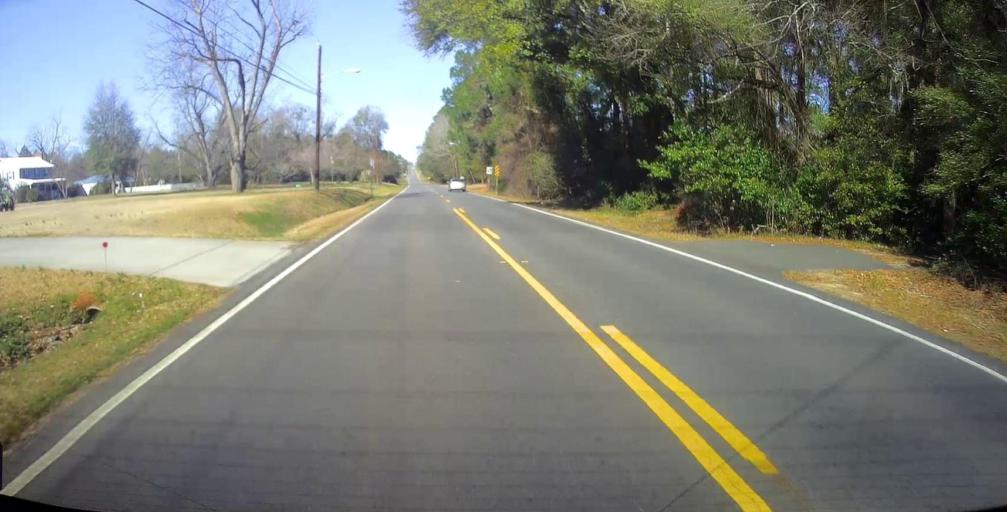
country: US
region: Georgia
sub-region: Macon County
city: Montezuma
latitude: 32.3184
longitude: -84.0233
